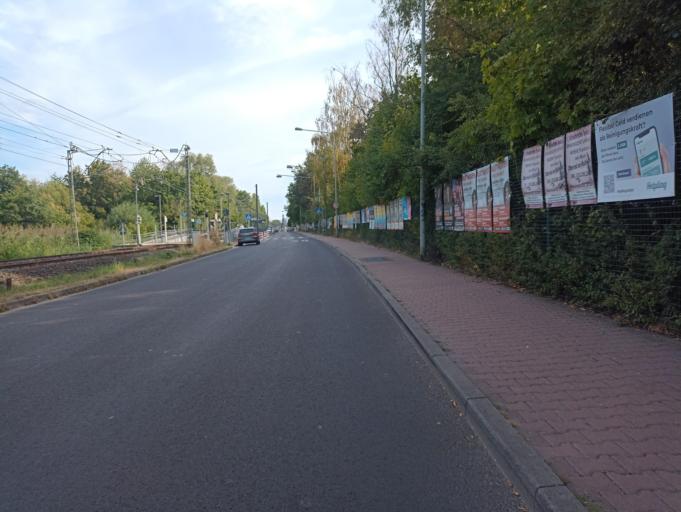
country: DE
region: Hesse
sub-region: Regierungsbezirk Darmstadt
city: Bad Homburg vor der Hoehe
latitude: 50.1722
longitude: 8.6425
